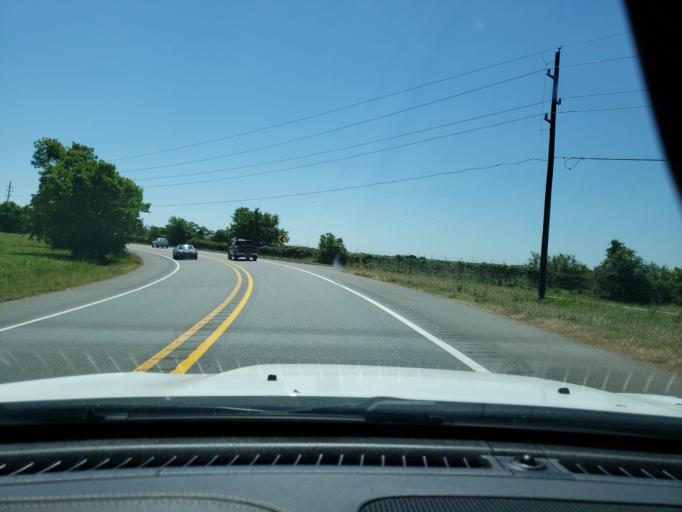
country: US
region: Texas
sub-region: Fort Bend County
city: Fulshear
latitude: 29.6856
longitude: -95.8454
